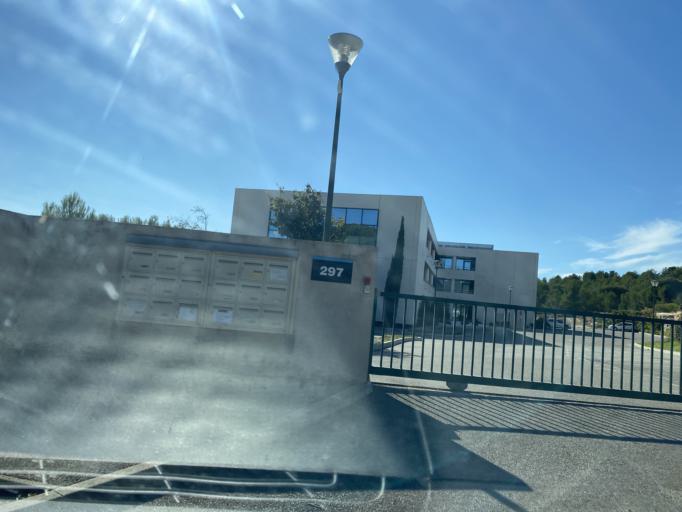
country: FR
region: Provence-Alpes-Cote d'Azur
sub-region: Departement des Bouches-du-Rhone
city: Ceyreste
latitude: 43.2088
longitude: 5.5990
